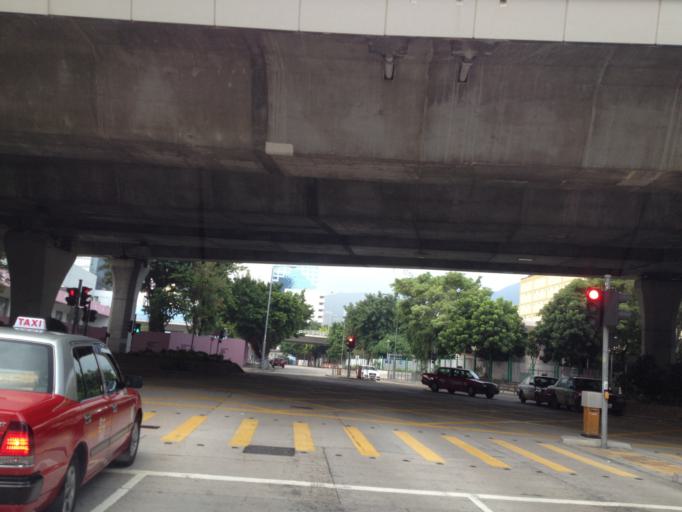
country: HK
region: Kowloon City
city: Kowloon
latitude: 22.3167
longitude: 114.2117
